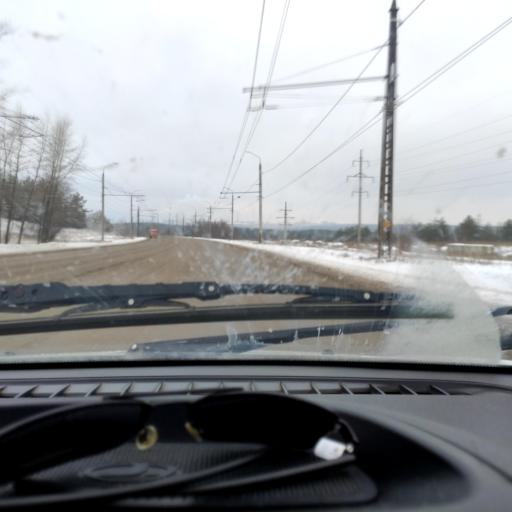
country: RU
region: Samara
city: Zhigulevsk
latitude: 53.5092
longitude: 49.5205
